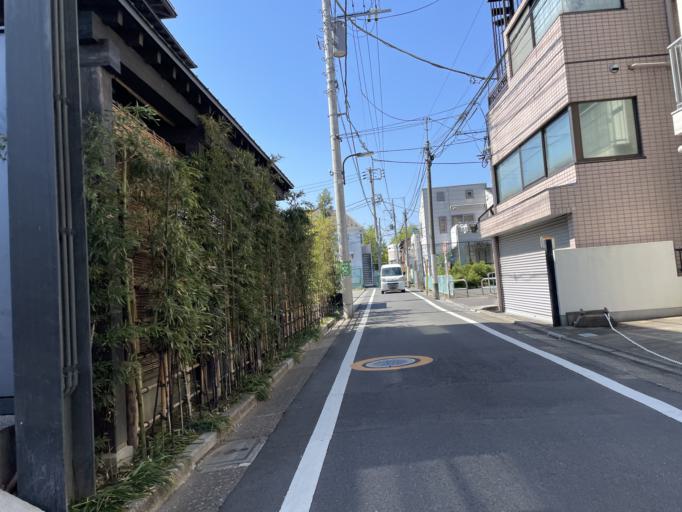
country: JP
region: Tokyo
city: Tokyo
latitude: 35.7406
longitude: 139.7384
